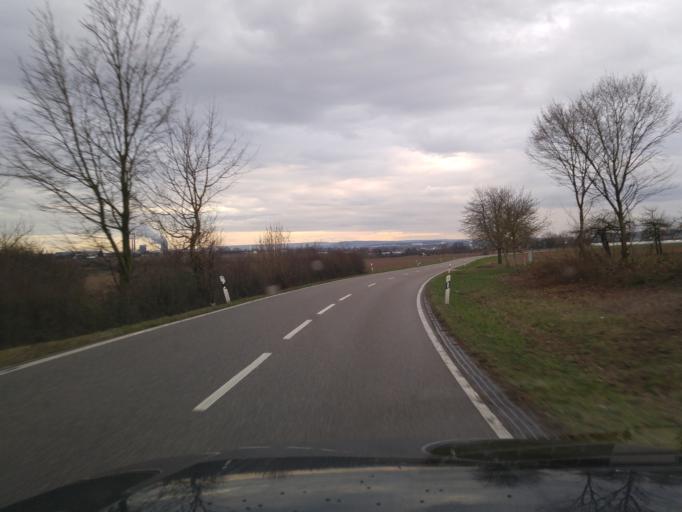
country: DE
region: Baden-Wuerttemberg
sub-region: Regierungsbezirk Stuttgart
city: Oedheim
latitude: 49.2318
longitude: 9.2478
